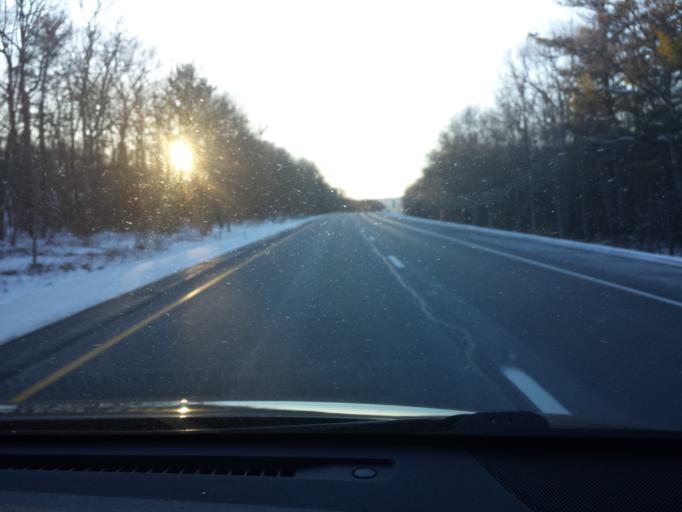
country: US
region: Pennsylvania
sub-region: Clinton County
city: Avis
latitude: 41.0554
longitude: -77.2773
